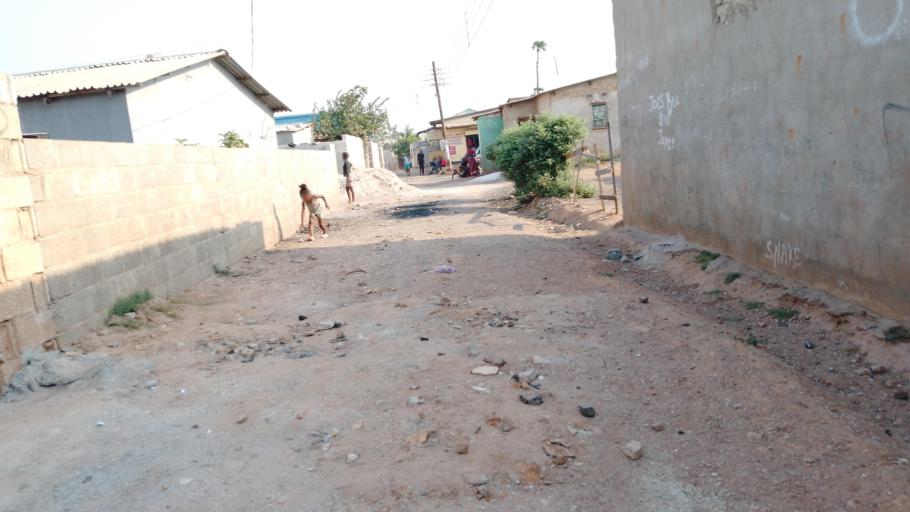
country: ZM
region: Lusaka
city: Lusaka
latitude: -15.3996
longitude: 28.3728
